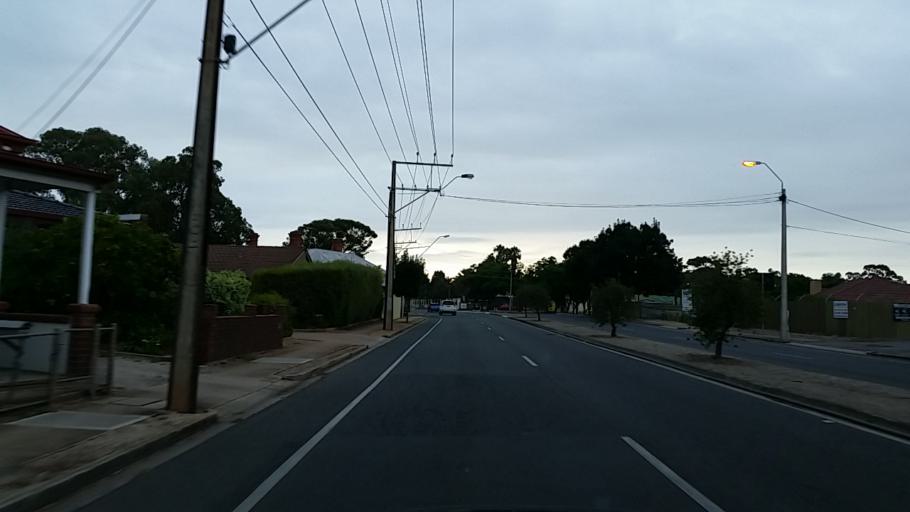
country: AU
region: South Australia
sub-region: Campbelltown
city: Paradise
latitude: -34.8705
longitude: 138.6738
